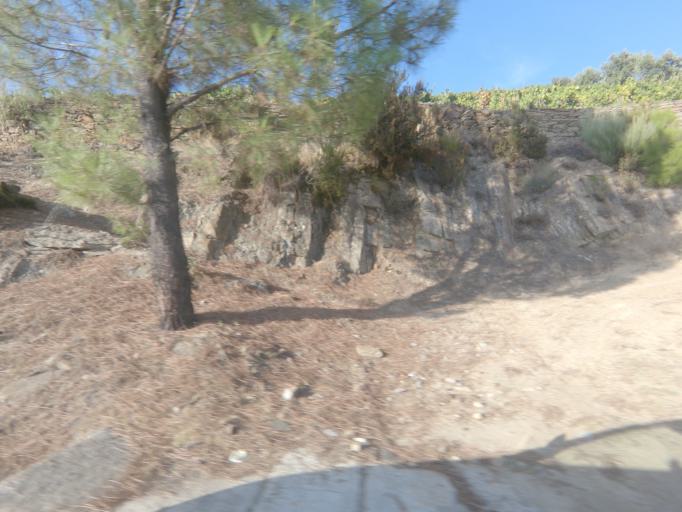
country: PT
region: Vila Real
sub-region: Sabrosa
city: Sabrosa
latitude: 41.2333
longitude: -7.5237
